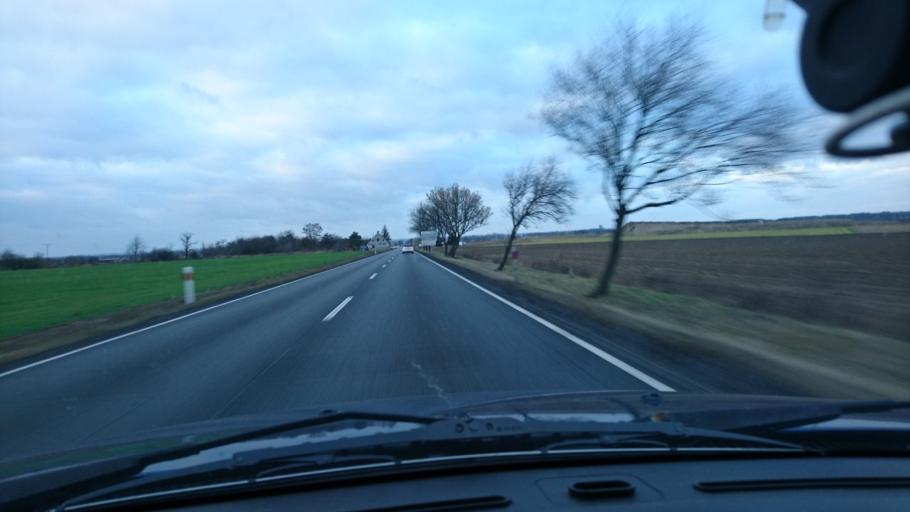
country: PL
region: Greater Poland Voivodeship
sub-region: Powiat kepinski
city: Baranow
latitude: 51.2525
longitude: 18.0135
